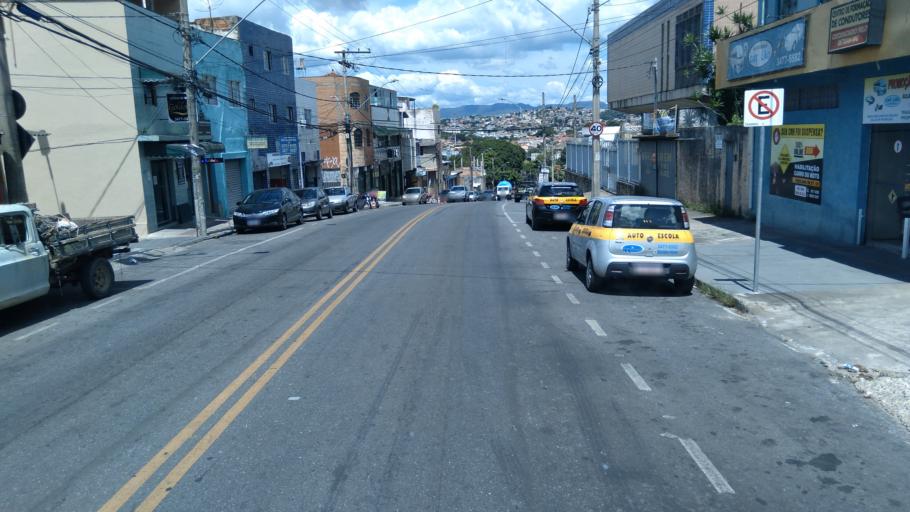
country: BR
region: Minas Gerais
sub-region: Contagem
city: Contagem
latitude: -19.8899
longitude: -44.0121
